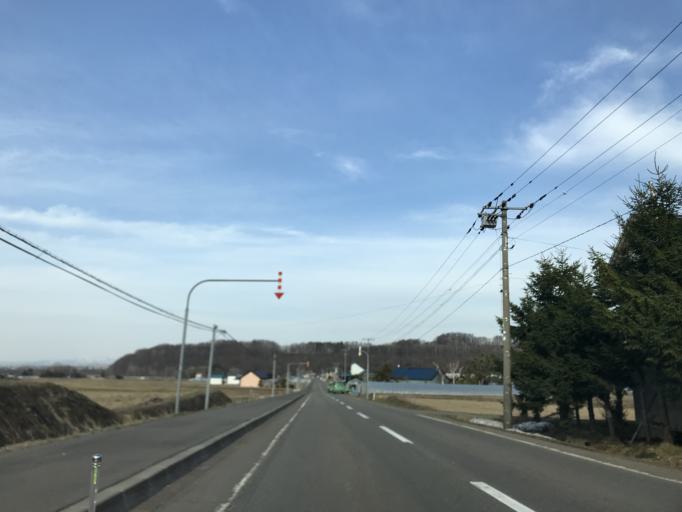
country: JP
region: Hokkaido
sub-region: Asahikawa-shi
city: Asahikawa
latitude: 43.7061
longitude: 142.3461
